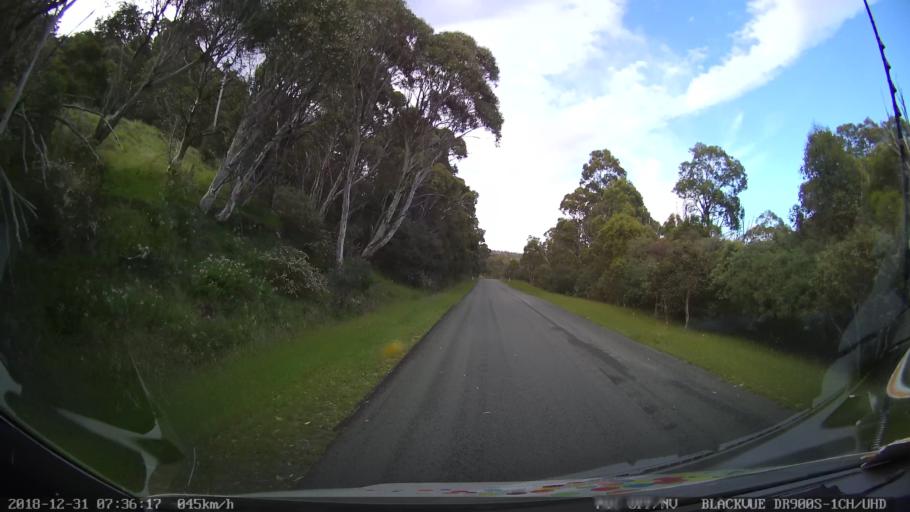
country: AU
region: New South Wales
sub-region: Snowy River
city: Jindabyne
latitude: -36.3400
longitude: 148.4434
